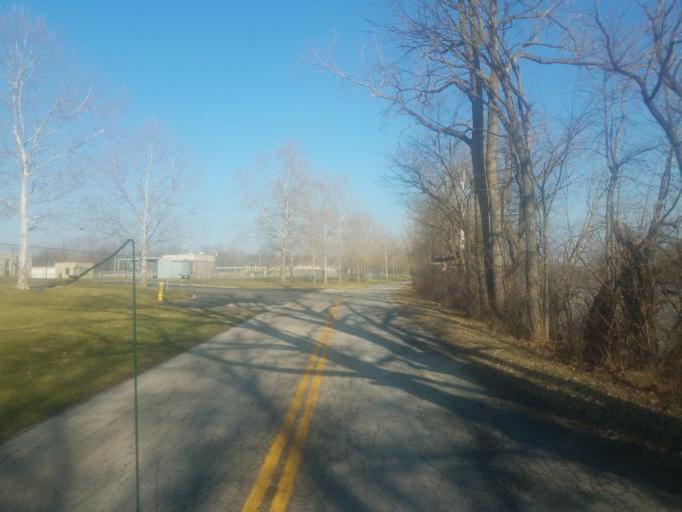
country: US
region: Ohio
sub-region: Seneca County
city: Tiffin
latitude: 41.1356
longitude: -83.1639
